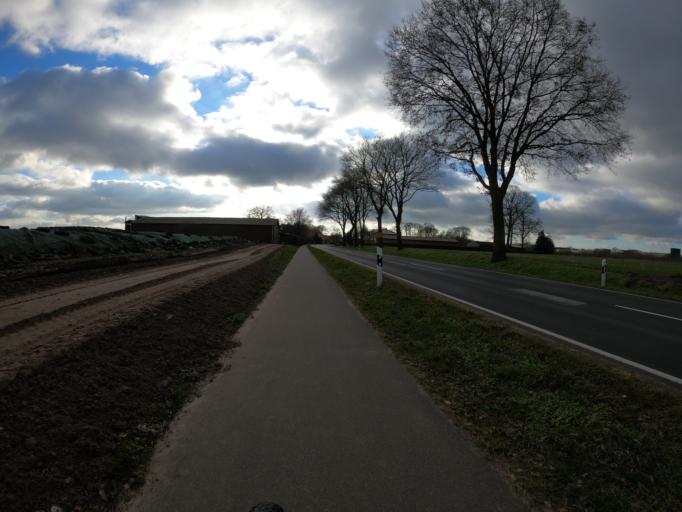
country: DE
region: Lower Saxony
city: Haselunne
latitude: 52.6583
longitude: 7.4466
